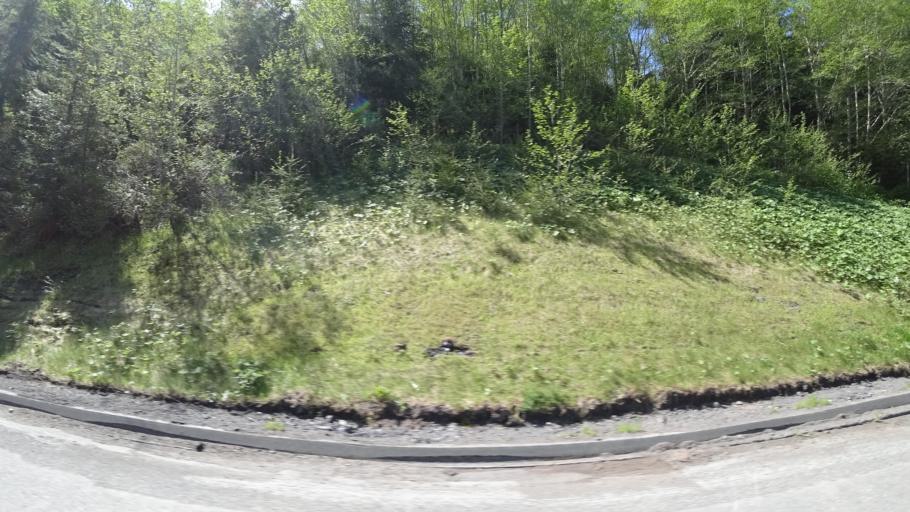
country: US
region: California
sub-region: Del Norte County
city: Bertsch-Oceanview
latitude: 41.4248
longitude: -124.0055
